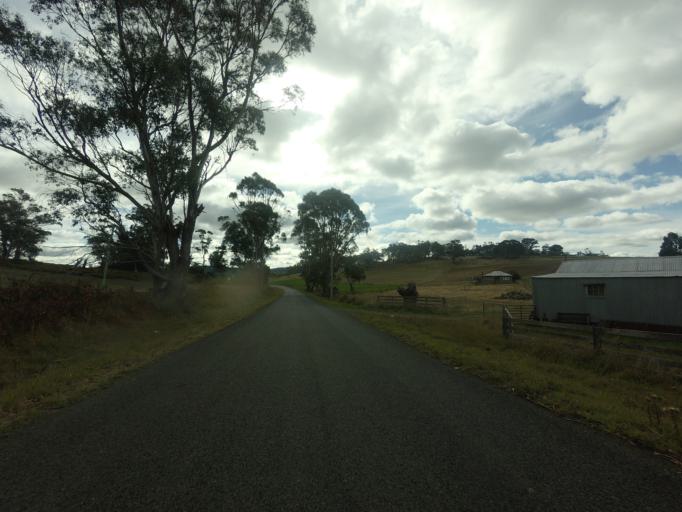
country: AU
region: Tasmania
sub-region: Brighton
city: Bridgewater
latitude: -42.4117
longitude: 147.4069
